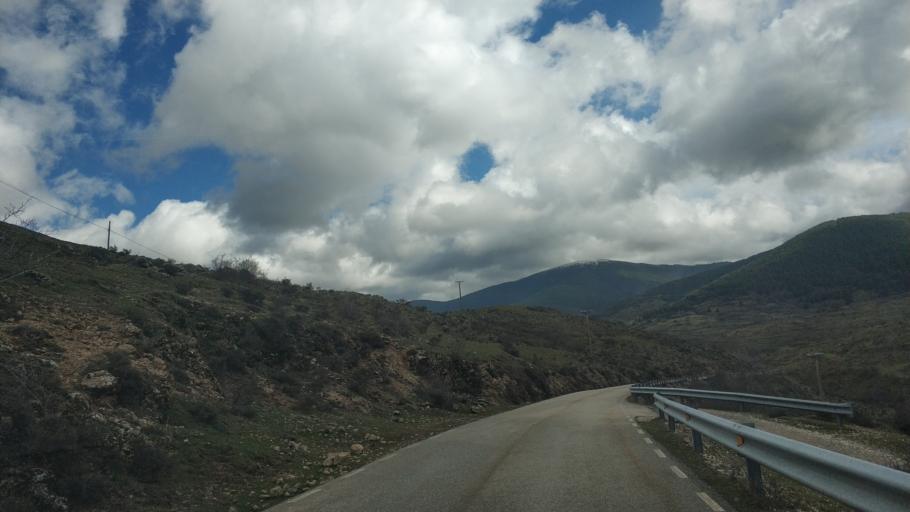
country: ES
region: Castille and Leon
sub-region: Provincia de Burgos
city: Neila
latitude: 42.0583
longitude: -3.0040
